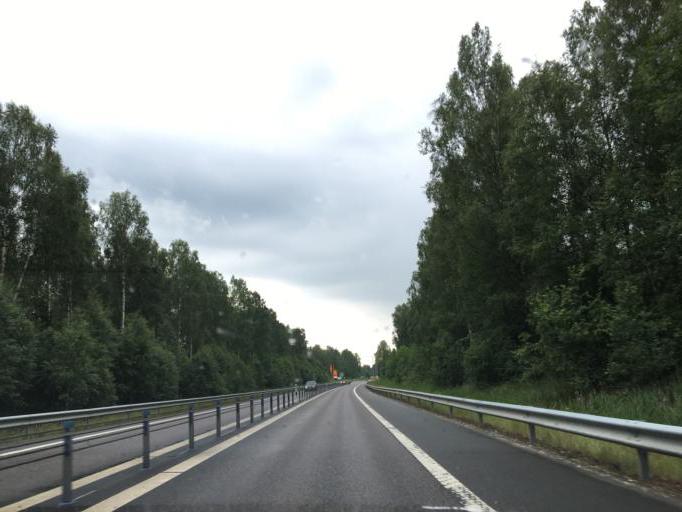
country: SE
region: OEstergoetland
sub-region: Norrkopings Kommun
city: Jursla
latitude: 58.7913
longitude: 16.1562
